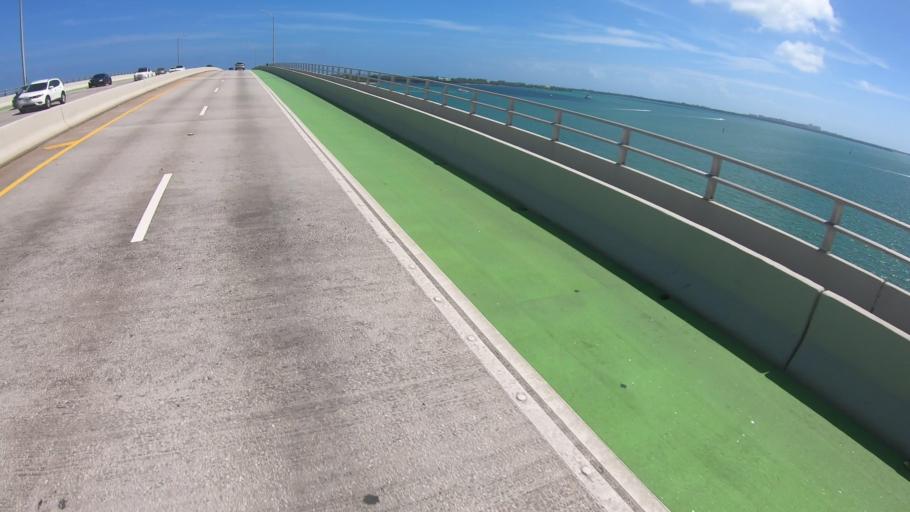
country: US
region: Florida
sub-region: Miami-Dade County
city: Miami
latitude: 25.7462
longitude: -80.1866
